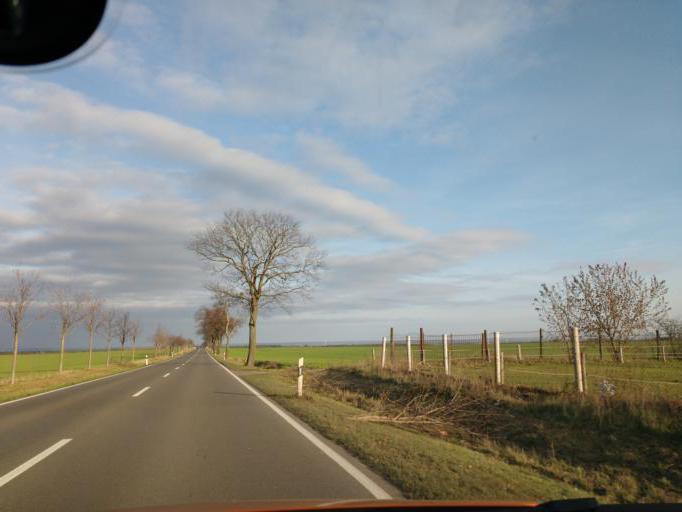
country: DE
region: Brandenburg
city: Wriezen
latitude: 52.6937
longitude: 14.1060
